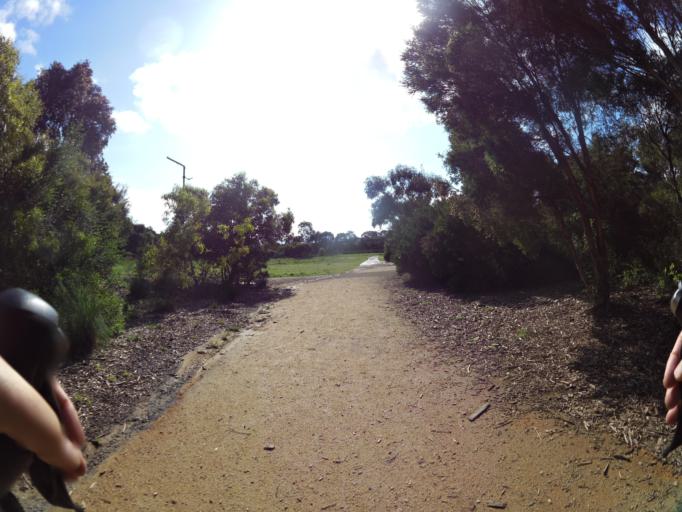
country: AU
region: Victoria
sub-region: Boroondara
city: Hawthorn East
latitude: -37.8283
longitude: 145.0499
